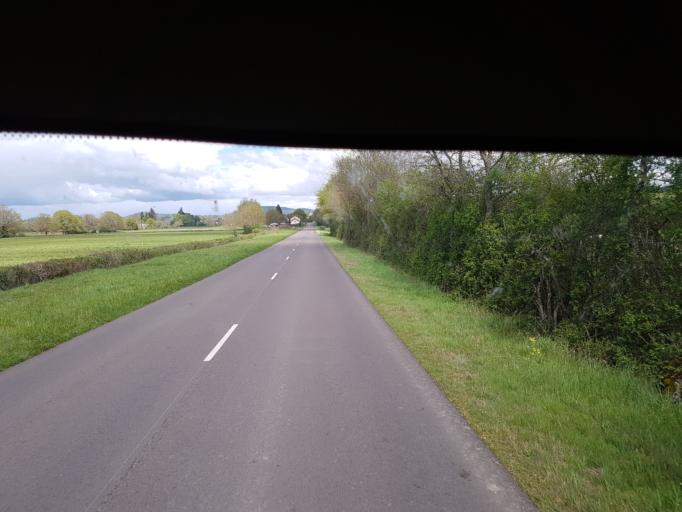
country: FR
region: Bourgogne
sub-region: Departement de Saone-et-Loire
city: Etang-sur-Arroux
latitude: 46.8335
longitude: 4.1848
